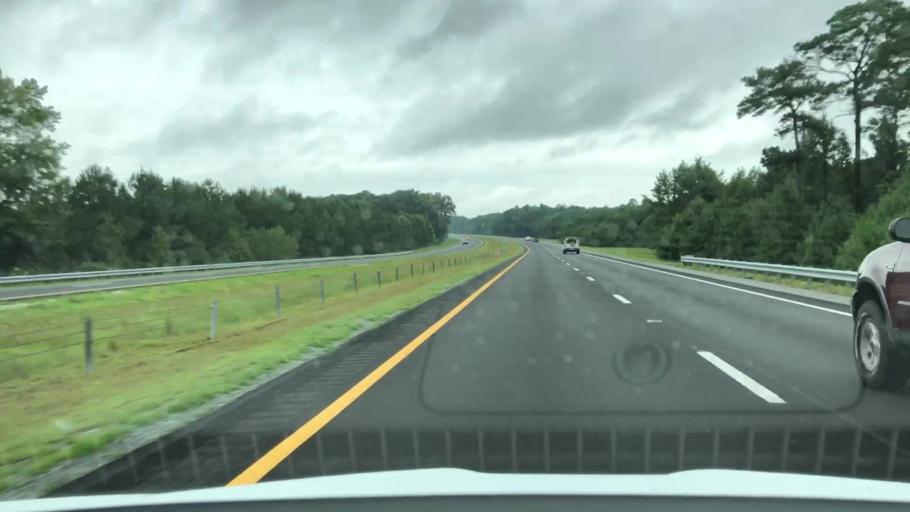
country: US
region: North Carolina
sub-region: Wayne County
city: Fremont
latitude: 35.4719
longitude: -77.9869
